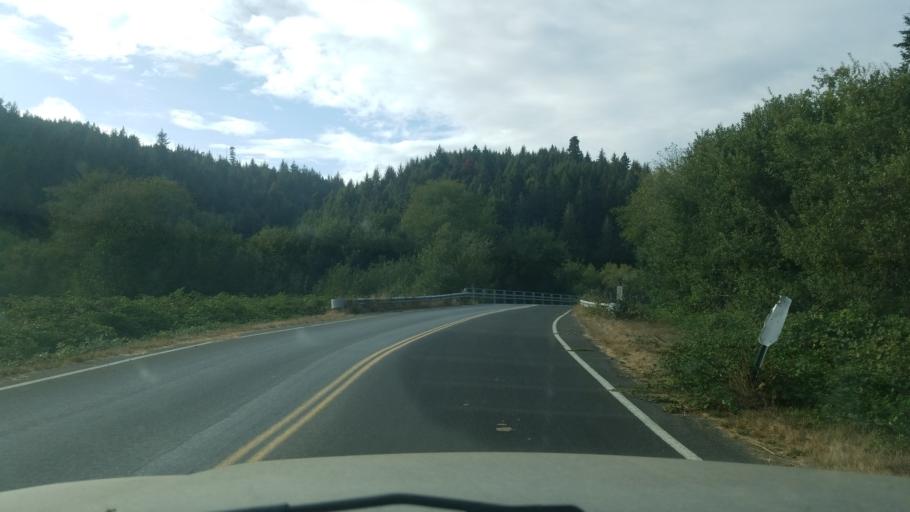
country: US
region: California
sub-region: Humboldt County
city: Westhaven-Moonstone
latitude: 41.3216
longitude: -124.0423
